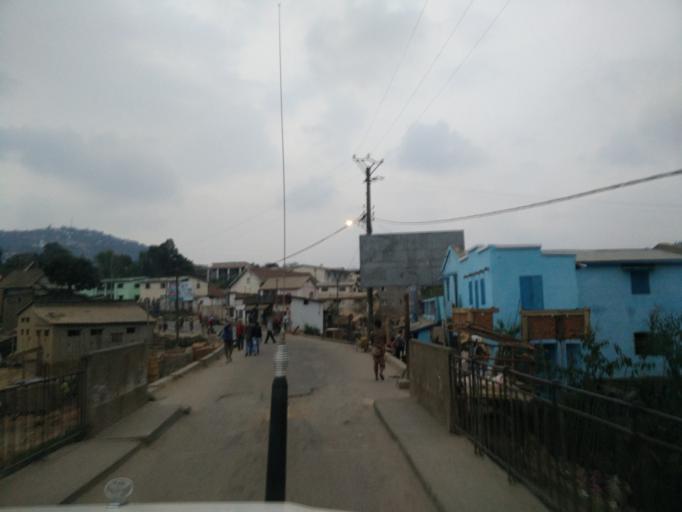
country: MG
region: Upper Matsiatra
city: Fianarantsoa
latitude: -21.4670
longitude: 47.0682
